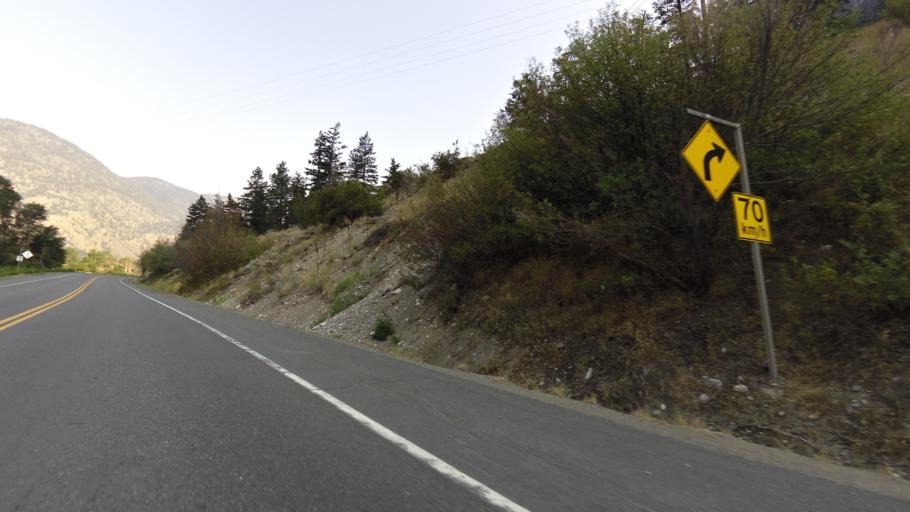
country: CA
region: British Columbia
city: Oliver
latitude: 49.2656
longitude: -120.0168
